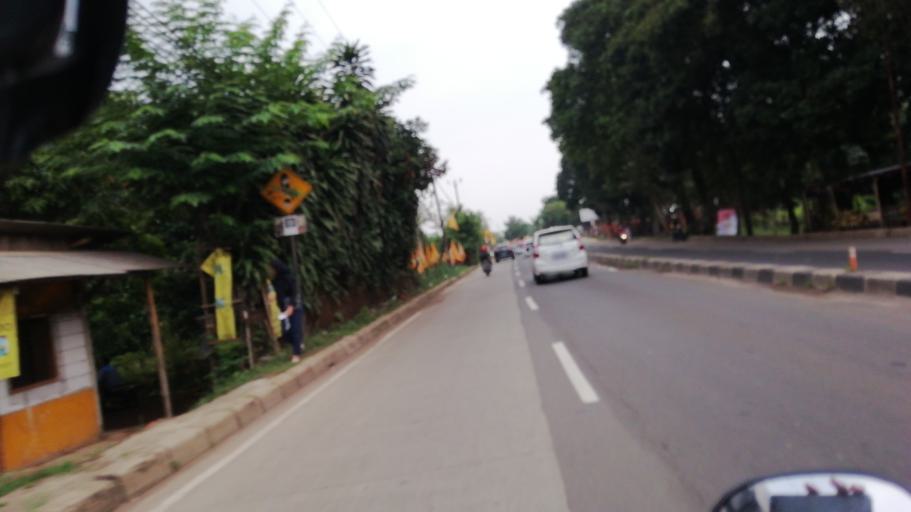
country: ID
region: West Java
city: Parung
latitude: -6.4935
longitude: 106.7465
